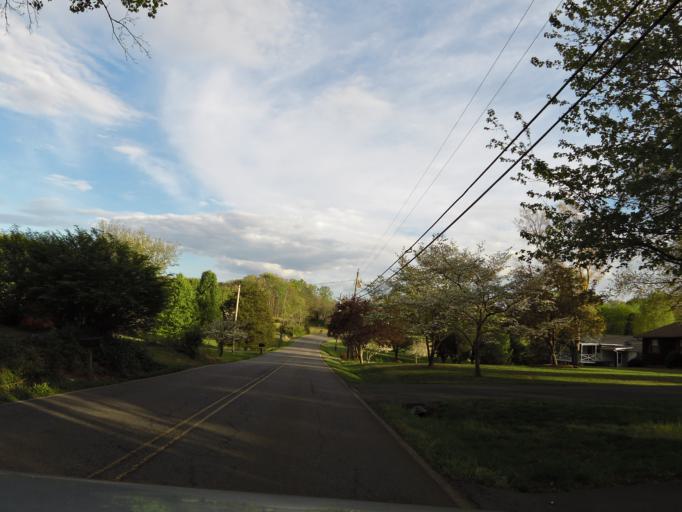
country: US
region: Tennessee
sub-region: Blount County
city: Maryville
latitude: 35.6822
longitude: -84.0133
